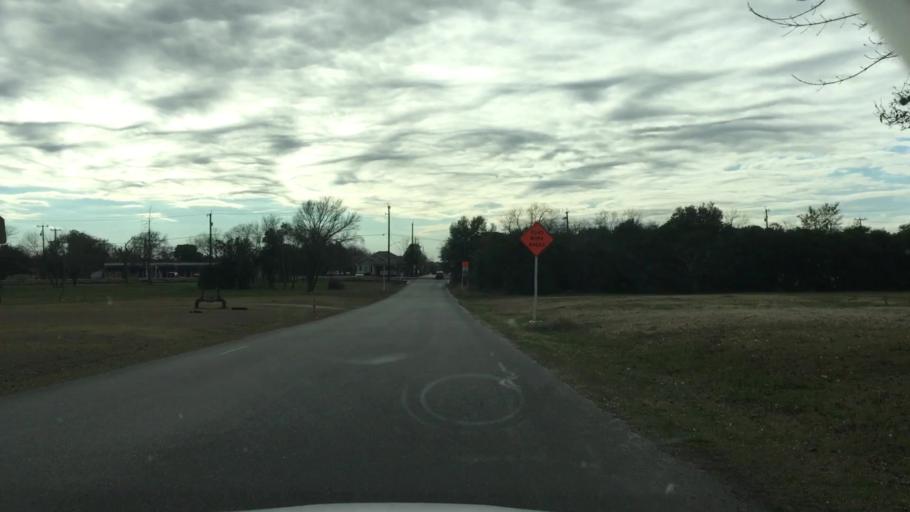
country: US
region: Texas
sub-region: Bexar County
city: Converse
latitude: 29.5172
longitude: -98.3109
